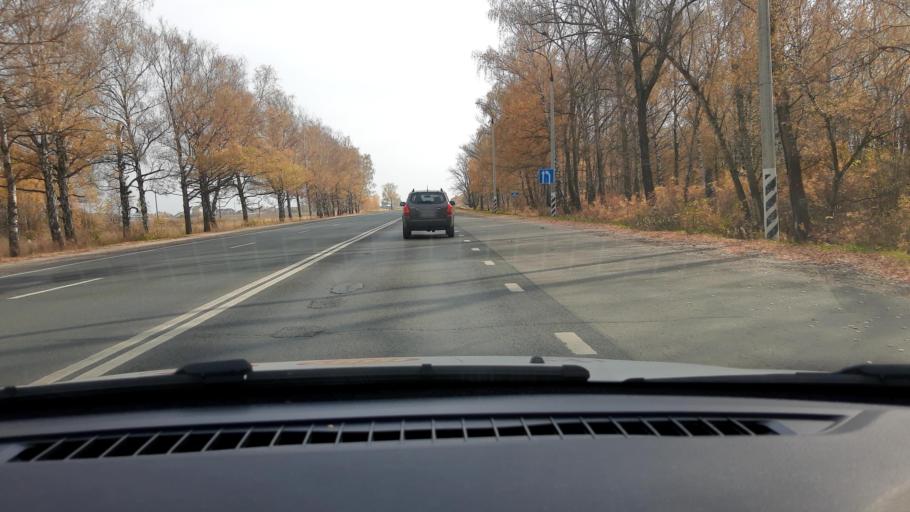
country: RU
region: Nizjnij Novgorod
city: Kstovo
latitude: 56.1356
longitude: 44.2411
